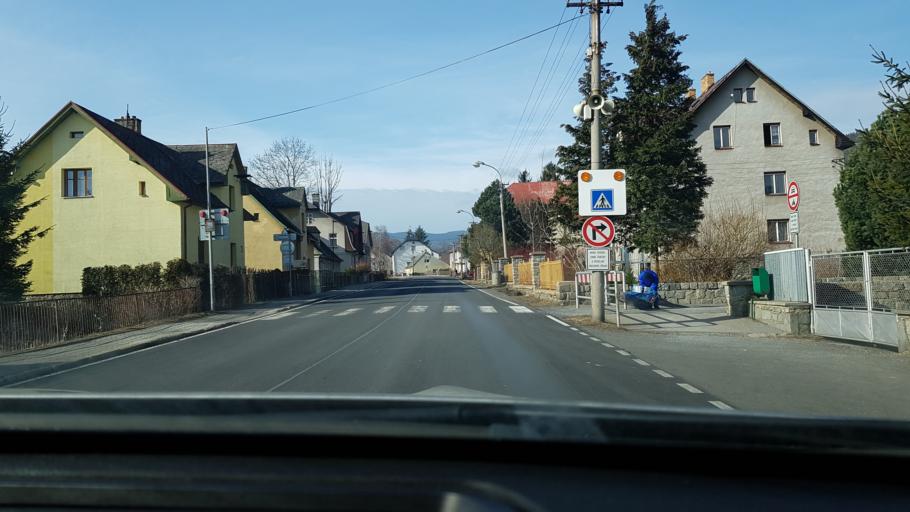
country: CZ
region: Olomoucky
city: Vapenna
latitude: 50.2271
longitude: 17.1344
